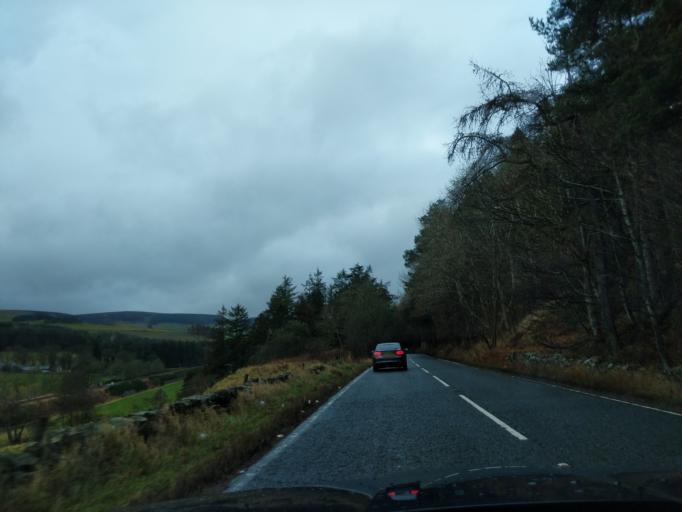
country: GB
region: Scotland
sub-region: The Scottish Borders
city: Galashiels
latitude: 55.6483
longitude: -2.8590
